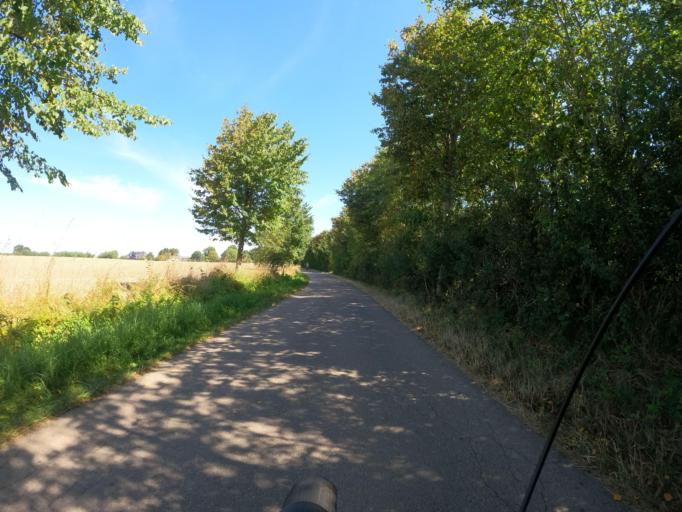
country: DE
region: Schleswig-Holstein
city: Steinbergkirche
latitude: 54.7991
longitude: 9.7430
